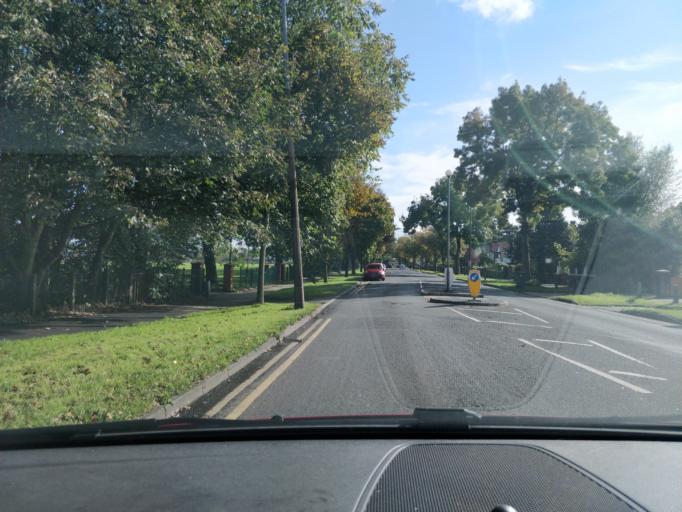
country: GB
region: England
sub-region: Sefton
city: Southport
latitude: 53.6353
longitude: -2.9769
